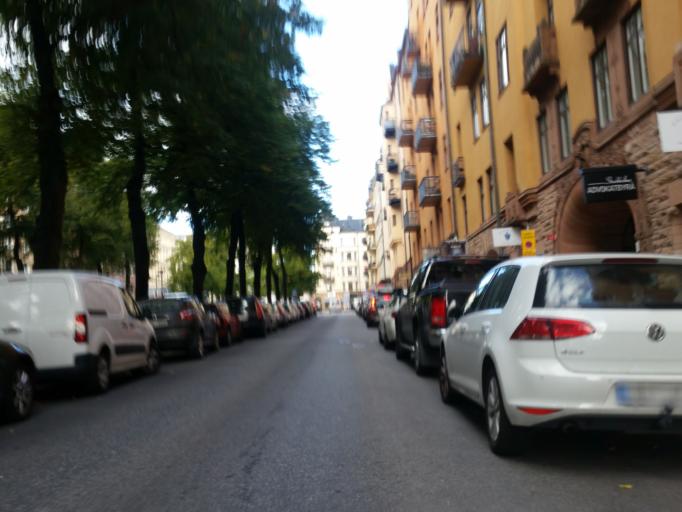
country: SE
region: Stockholm
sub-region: Stockholms Kommun
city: Stockholm
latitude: 59.3274
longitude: 18.0425
